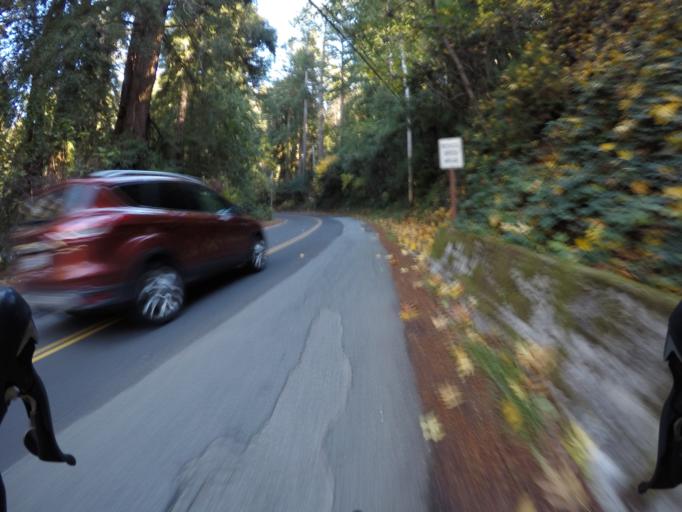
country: US
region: California
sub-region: Santa Cruz County
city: Mount Hermon
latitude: 37.0488
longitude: -122.0625
